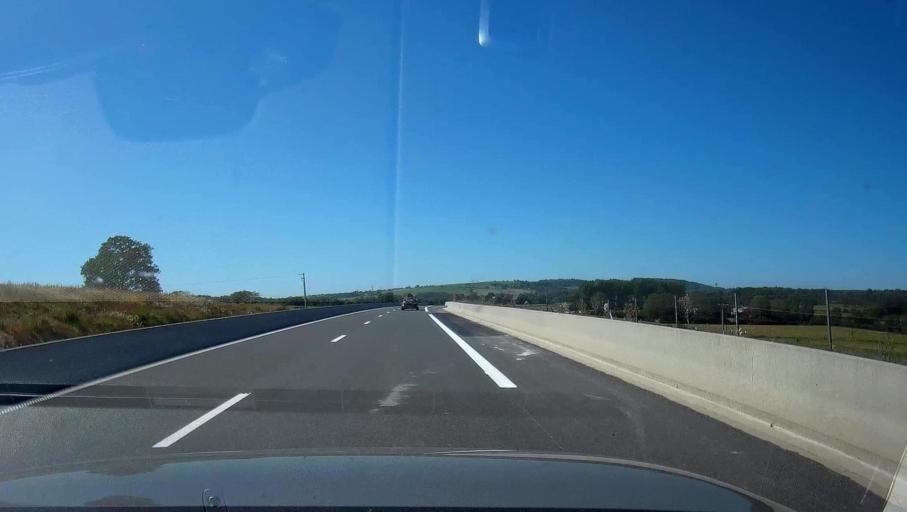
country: FR
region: Champagne-Ardenne
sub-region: Departement des Ardennes
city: Rimogne
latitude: 49.7909
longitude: 4.5505
